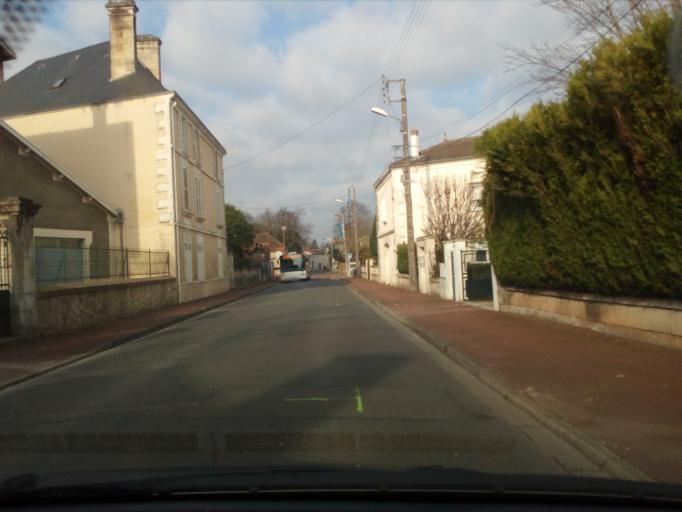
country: FR
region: Poitou-Charentes
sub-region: Departement de la Charente
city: Gond-Pontouvre
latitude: 45.6656
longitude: 0.1619
